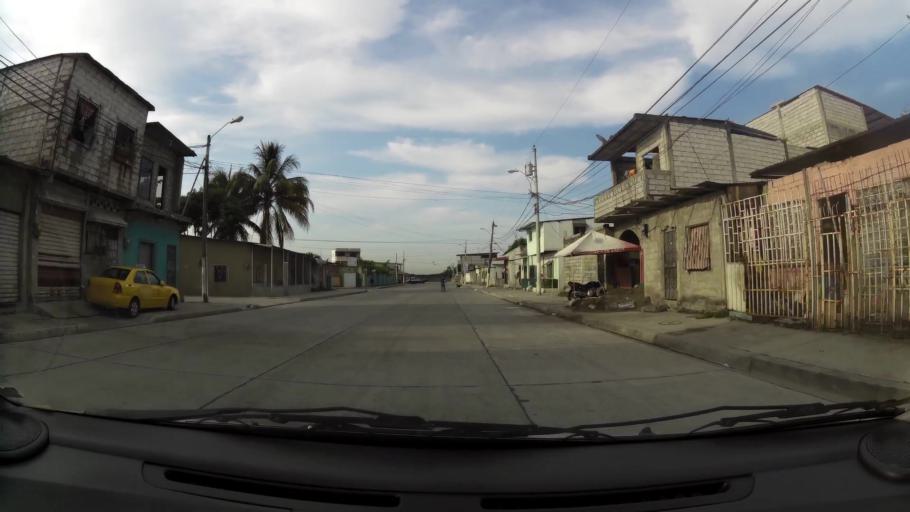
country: EC
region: Guayas
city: Eloy Alfaro
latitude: -2.0906
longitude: -79.8975
